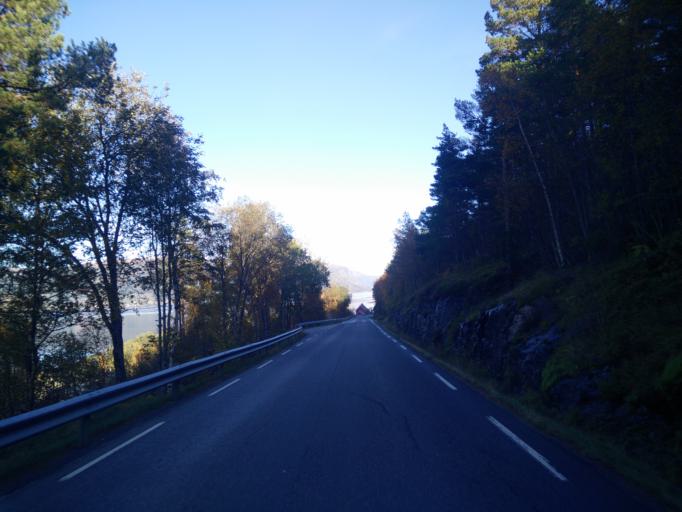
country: NO
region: More og Romsdal
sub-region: Halsa
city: Liaboen
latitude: 63.1325
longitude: 8.3904
